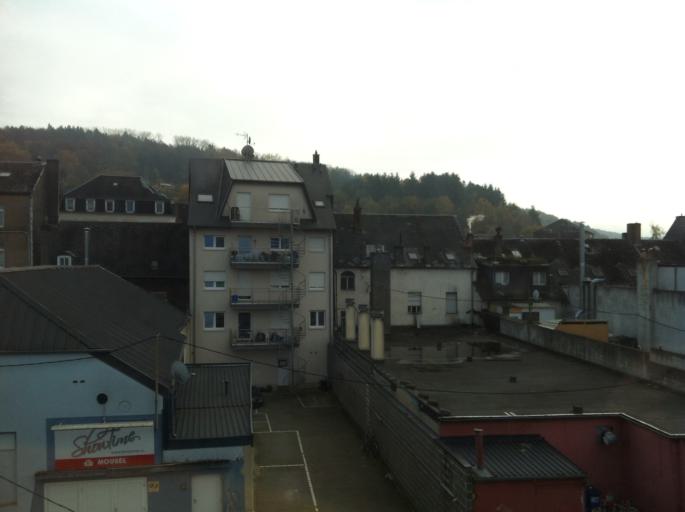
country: LU
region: Luxembourg
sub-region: Canton d'Esch-sur-Alzette
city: Esch-sur-Alzette
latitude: 49.4900
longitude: 5.9781
